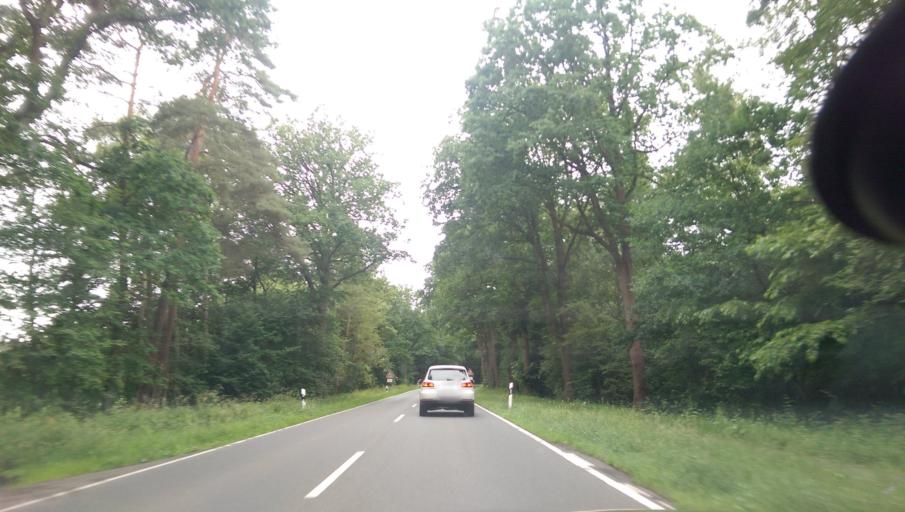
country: DE
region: Lower Saxony
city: Rotenburg
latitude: 53.0775
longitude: 9.4306
